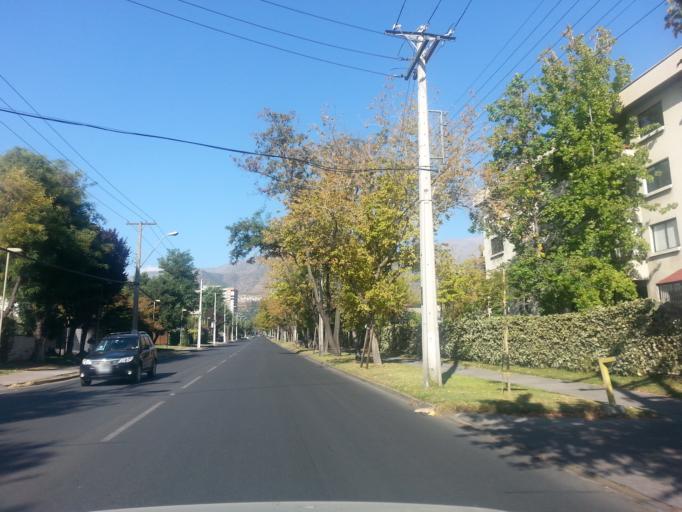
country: CL
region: Santiago Metropolitan
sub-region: Provincia de Santiago
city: Villa Presidente Frei, Nunoa, Santiago, Chile
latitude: -33.4246
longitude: -70.5455
